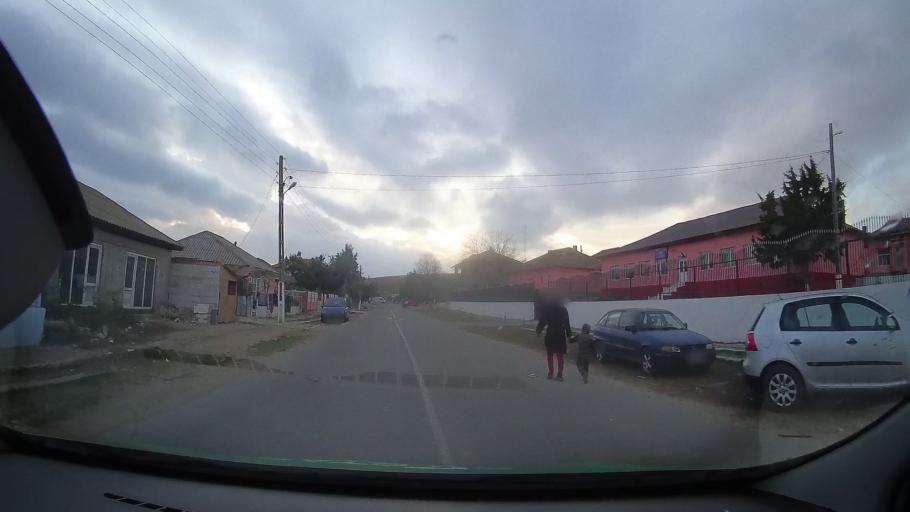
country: RO
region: Constanta
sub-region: Comuna Dobromir
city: Dobromir
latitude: 44.0216
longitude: 27.7829
